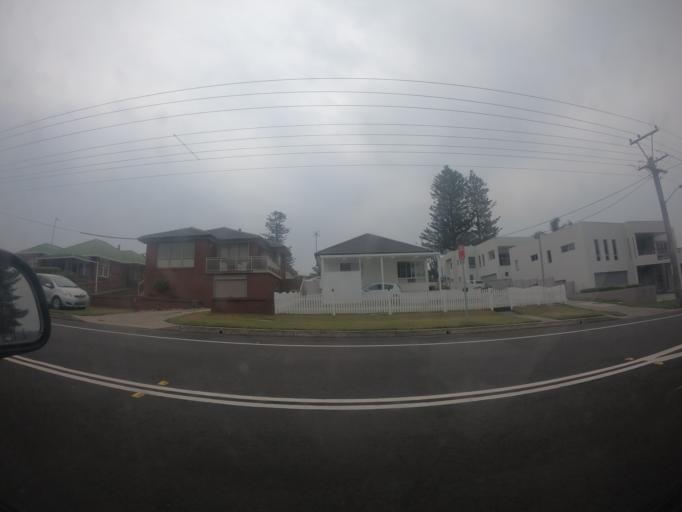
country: AU
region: New South Wales
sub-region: Shellharbour
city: Shellharbour Village
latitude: -34.5744
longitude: 150.8681
